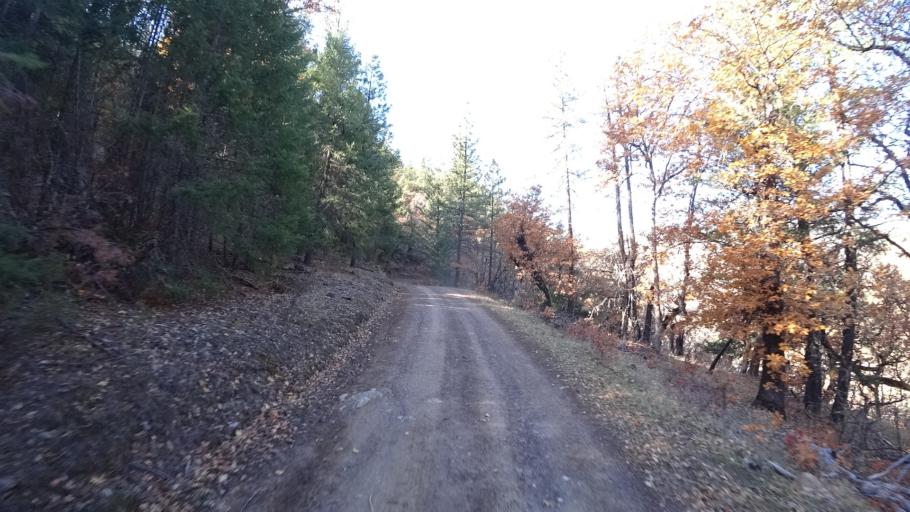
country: US
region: California
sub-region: Siskiyou County
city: Yreka
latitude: 41.8667
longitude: -122.8090
